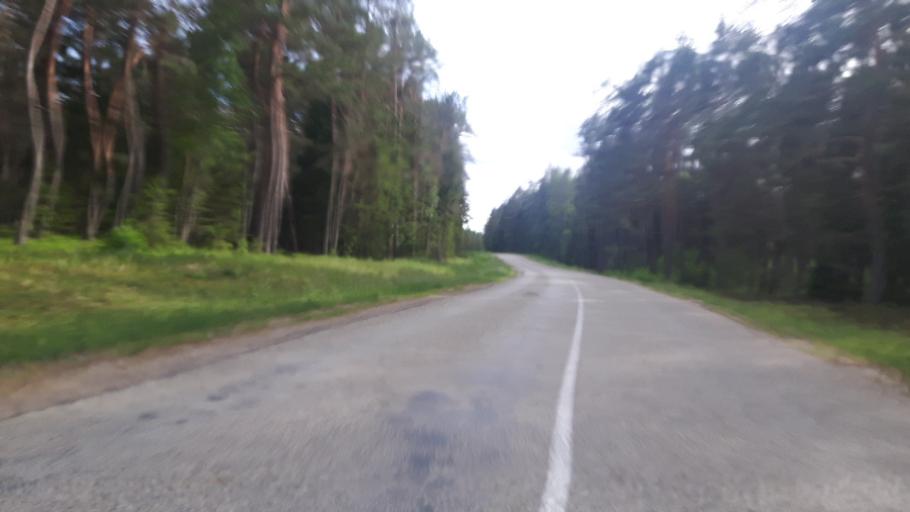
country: LV
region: Engure
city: Smarde
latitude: 57.0076
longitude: 23.3360
